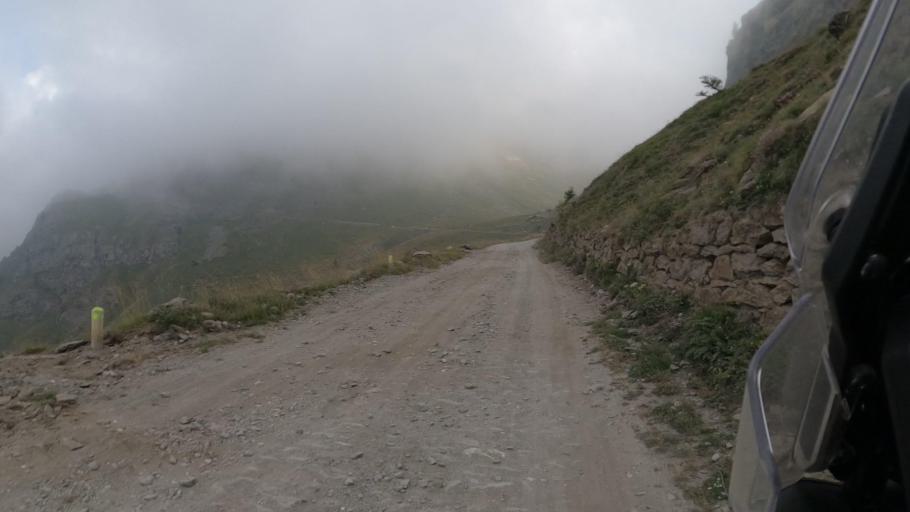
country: IT
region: Piedmont
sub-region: Provincia di Torino
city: Usseaux
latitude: 45.0614
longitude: 6.9773
